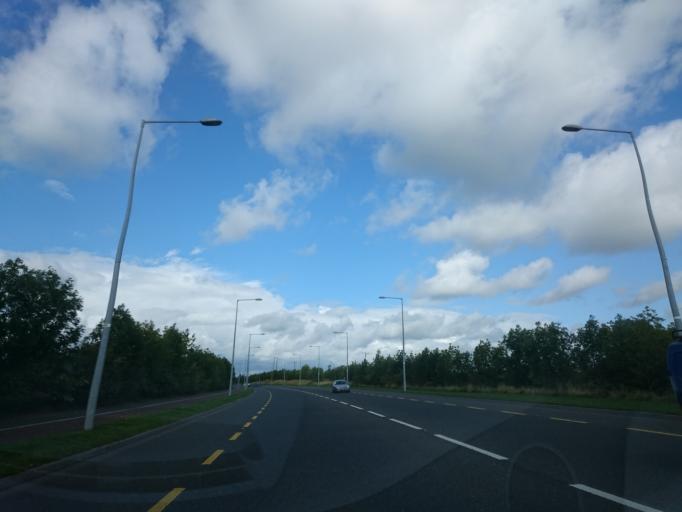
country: IE
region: Leinster
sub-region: Kilkenny
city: Kilkenny
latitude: 52.6731
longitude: -7.2335
